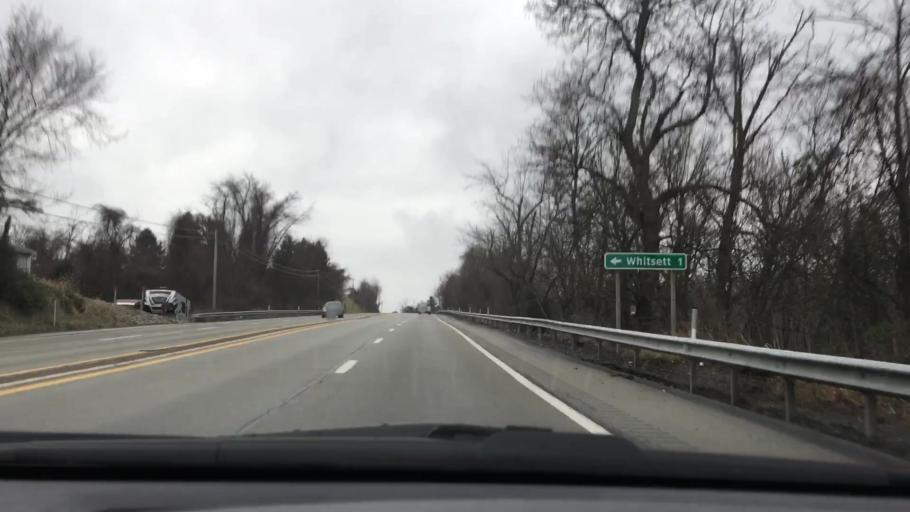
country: US
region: Pennsylvania
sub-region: Fayette County
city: Perryopolis
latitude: 40.1177
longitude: -79.7719
